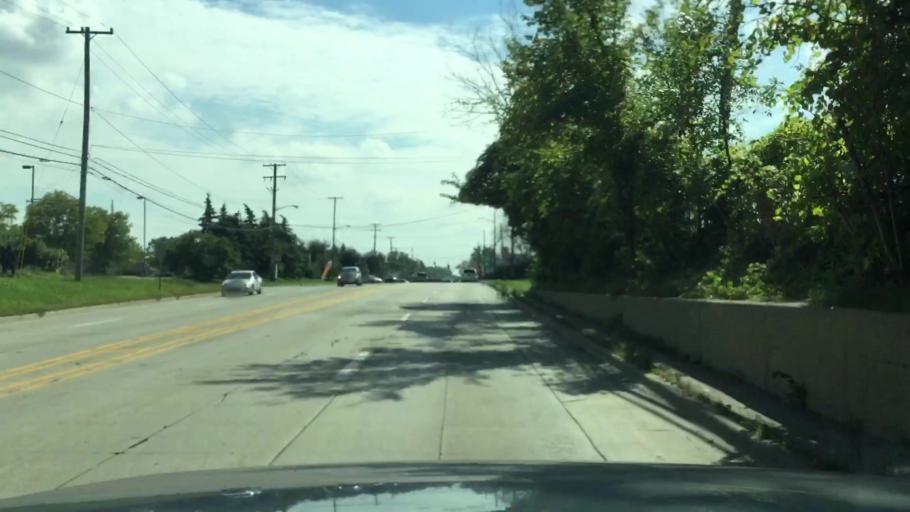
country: US
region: Michigan
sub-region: Wayne County
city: Wayne
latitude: 42.2882
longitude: -83.3489
